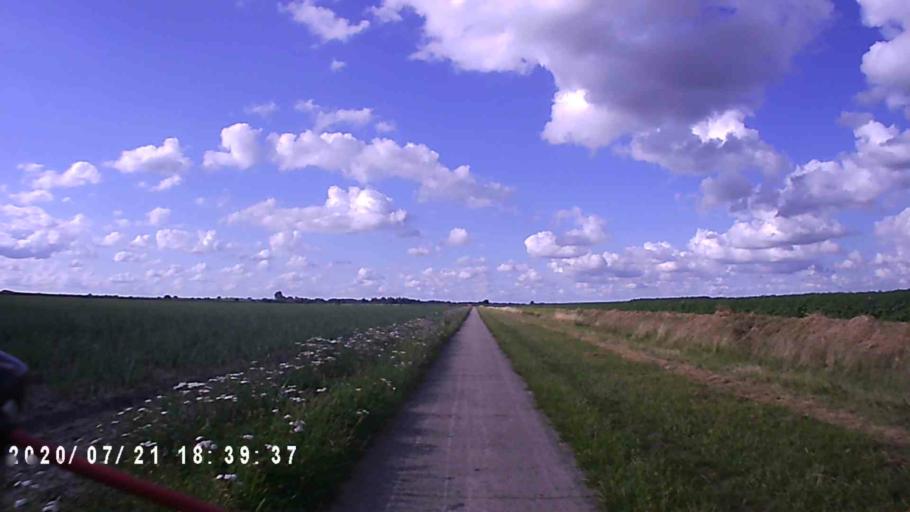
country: NL
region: Groningen
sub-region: Gemeente Hoogezand-Sappemeer
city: Hoogezand
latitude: 53.1958
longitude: 6.7485
